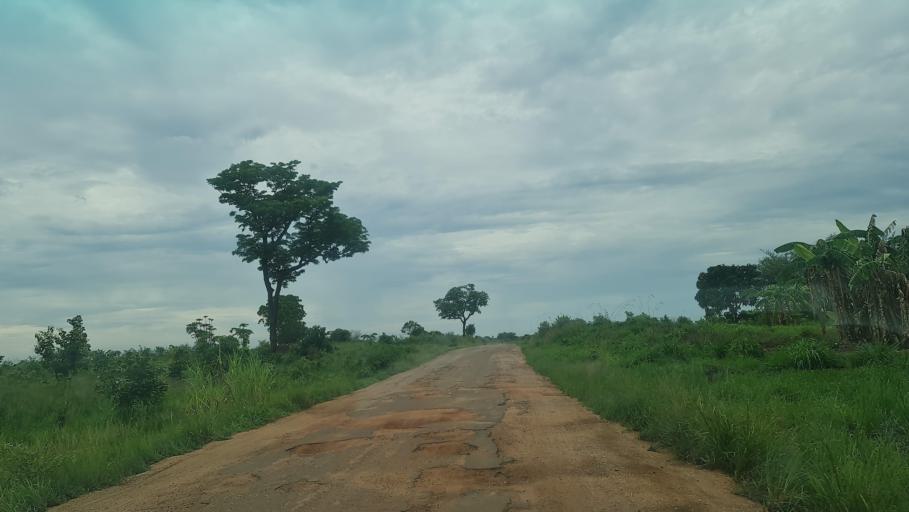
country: MW
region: Southern Region
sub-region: Nsanje District
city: Nsanje
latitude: -17.6855
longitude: 35.7281
